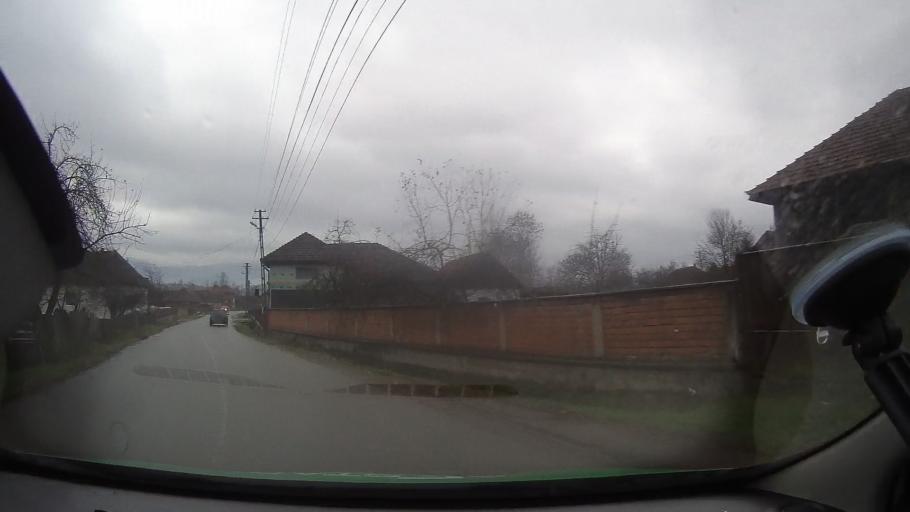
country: RO
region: Hunedoara
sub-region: Comuna Tomesti
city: Tomesti
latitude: 46.1977
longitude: 22.6424
